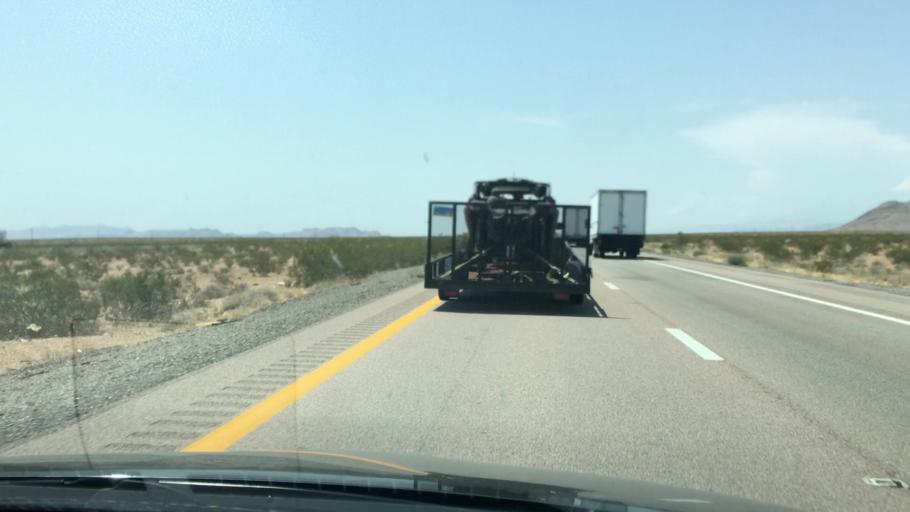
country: US
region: Nevada
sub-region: Clark County
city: Moapa Valley
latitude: 36.7282
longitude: -114.4484
